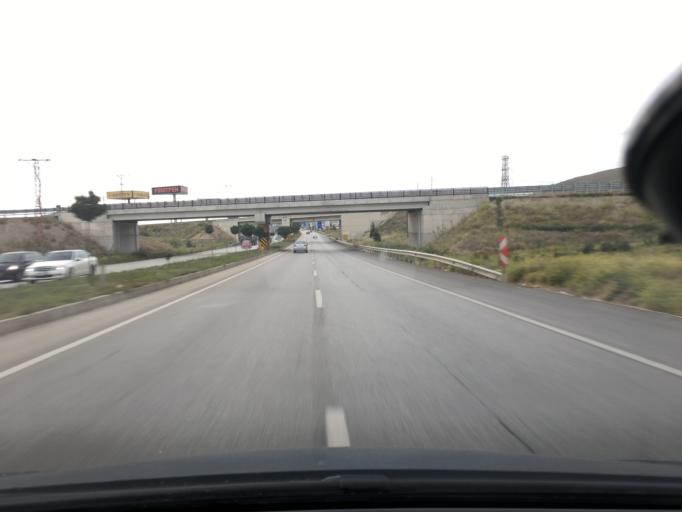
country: TR
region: Afyonkarahisar
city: Afyonkarahisar
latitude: 38.7944
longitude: 30.4022
